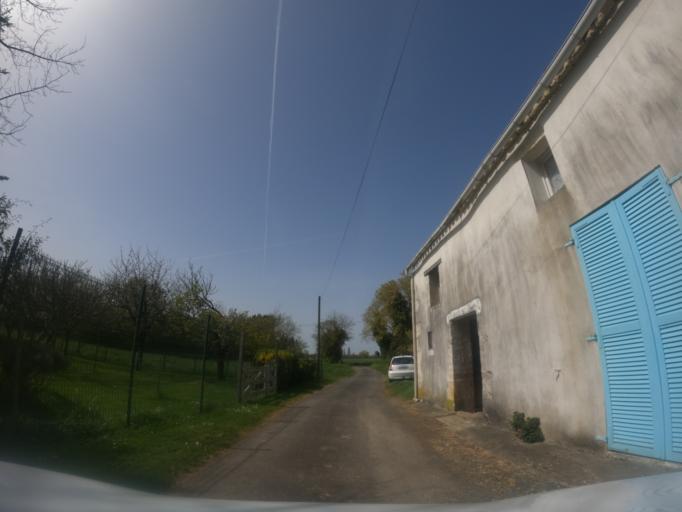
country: FR
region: Pays de la Loire
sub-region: Departement de la Vendee
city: Vix
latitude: 46.3919
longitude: -0.8254
